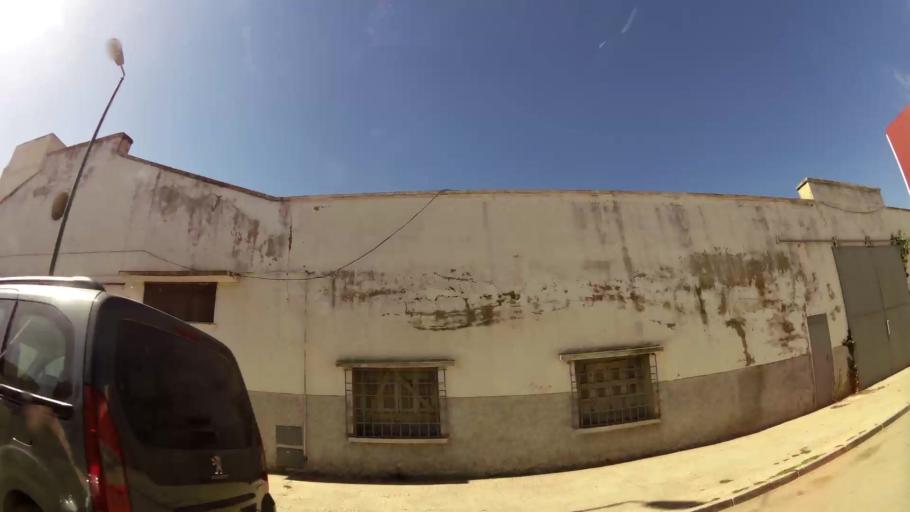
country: MA
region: Meknes-Tafilalet
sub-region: Meknes
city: Meknes
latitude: 33.8920
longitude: -5.5298
